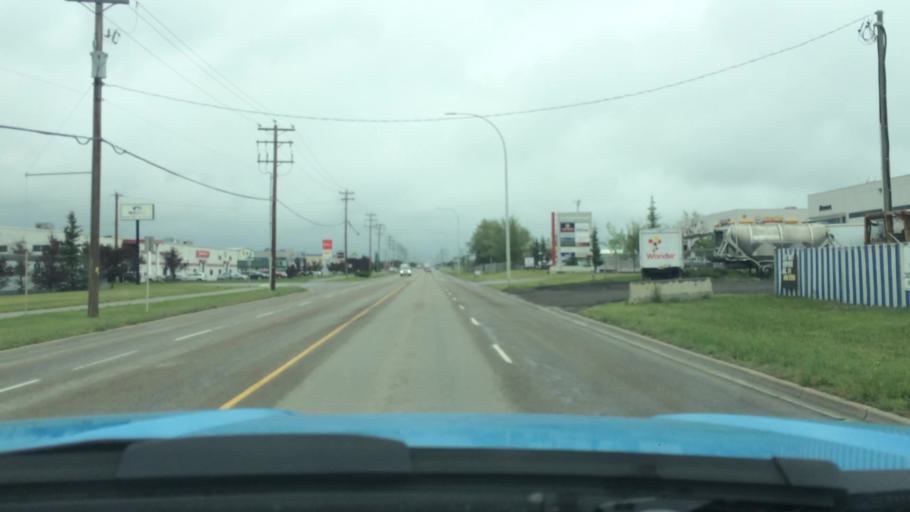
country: CA
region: Alberta
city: Airdrie
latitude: 51.2954
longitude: -113.9899
